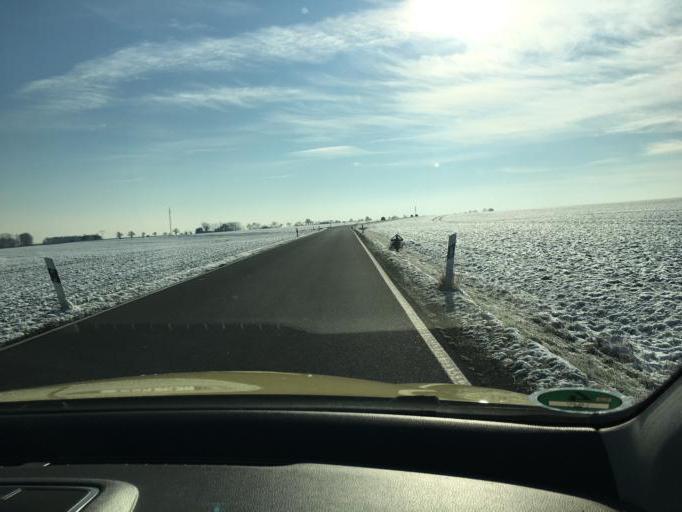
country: DE
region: Saxony
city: Belgershain
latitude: 51.2506
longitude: 12.5424
